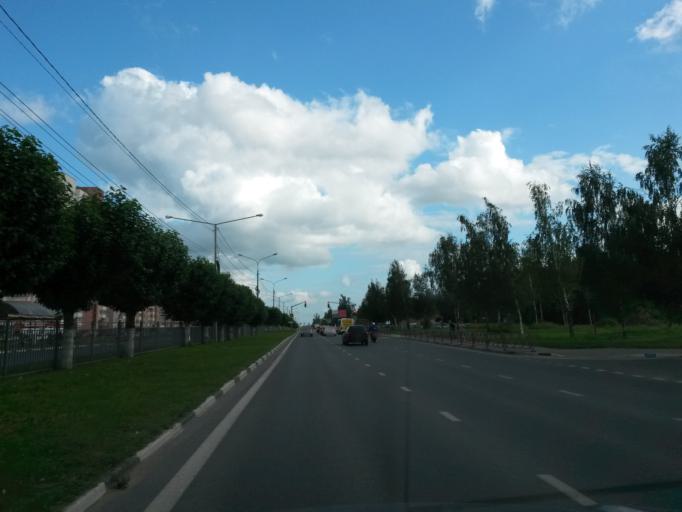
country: RU
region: Jaroslavl
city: Yaroslavl
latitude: 57.5847
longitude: 39.9069
